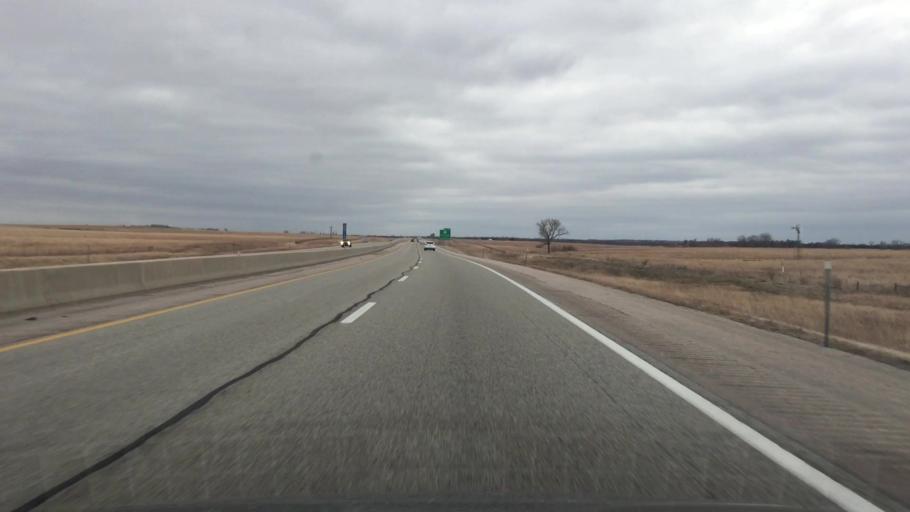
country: US
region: Kansas
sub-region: Butler County
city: El Dorado
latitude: 37.8965
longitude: -96.8347
